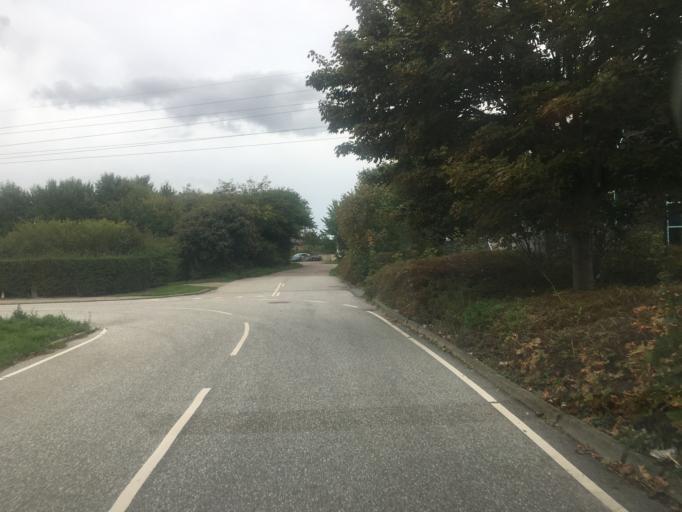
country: DK
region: South Denmark
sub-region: Tonder Kommune
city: Tonder
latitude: 54.9288
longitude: 8.8570
